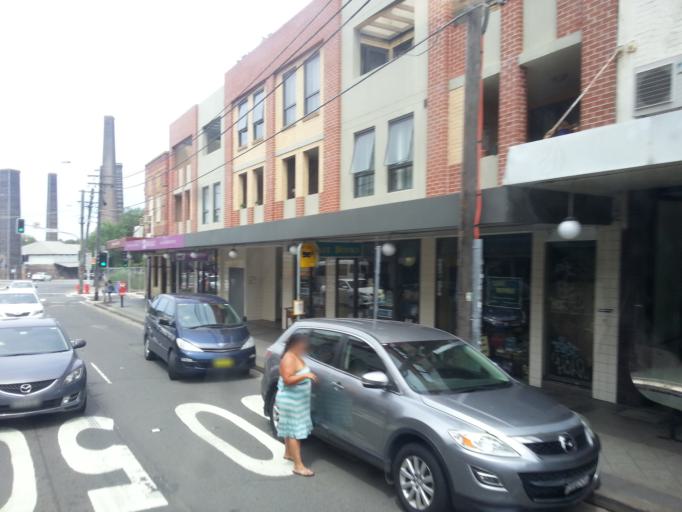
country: AU
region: New South Wales
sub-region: Marrickville
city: Newtown
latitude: -33.9064
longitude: 151.1812
